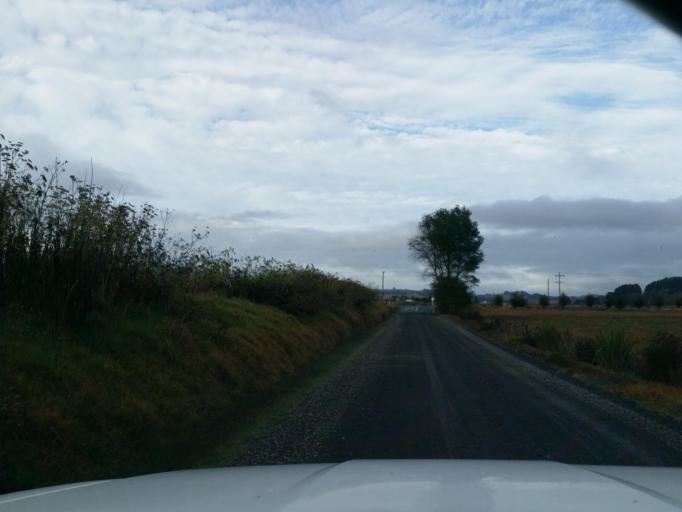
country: NZ
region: Northland
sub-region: Kaipara District
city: Dargaville
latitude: -35.9949
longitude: 173.8882
